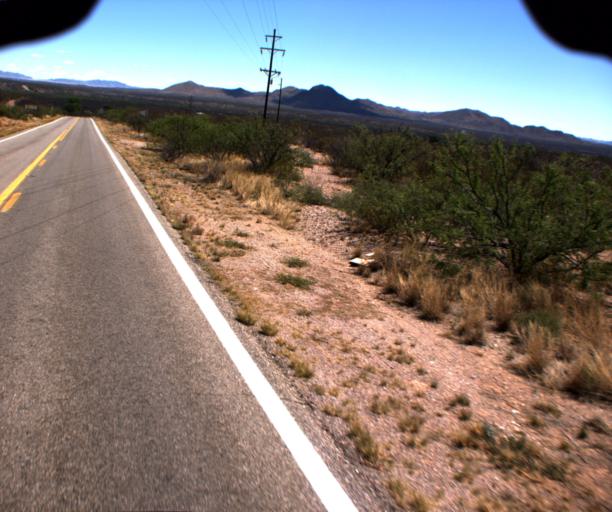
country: US
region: Arizona
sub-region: Cochise County
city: Tombstone
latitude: 31.7227
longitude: -110.2030
